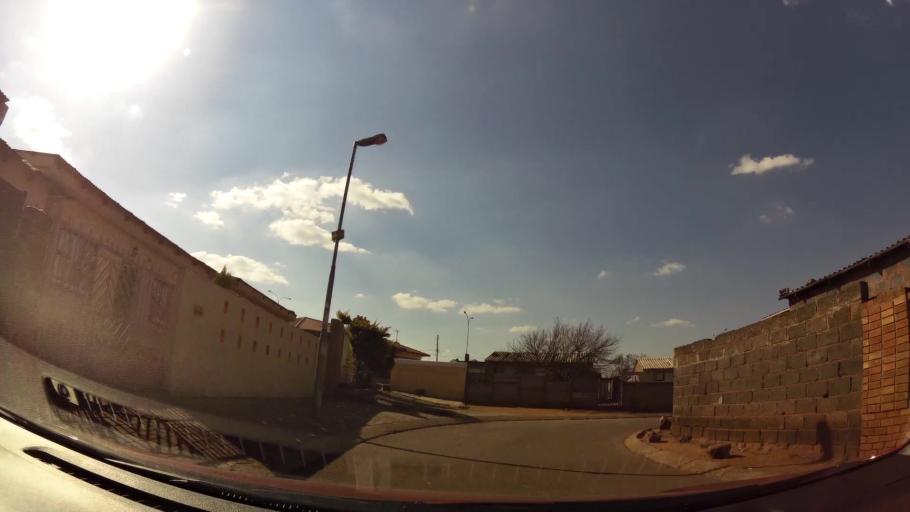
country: ZA
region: Gauteng
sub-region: City of Johannesburg Metropolitan Municipality
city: Soweto
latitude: -26.2341
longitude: 27.8757
